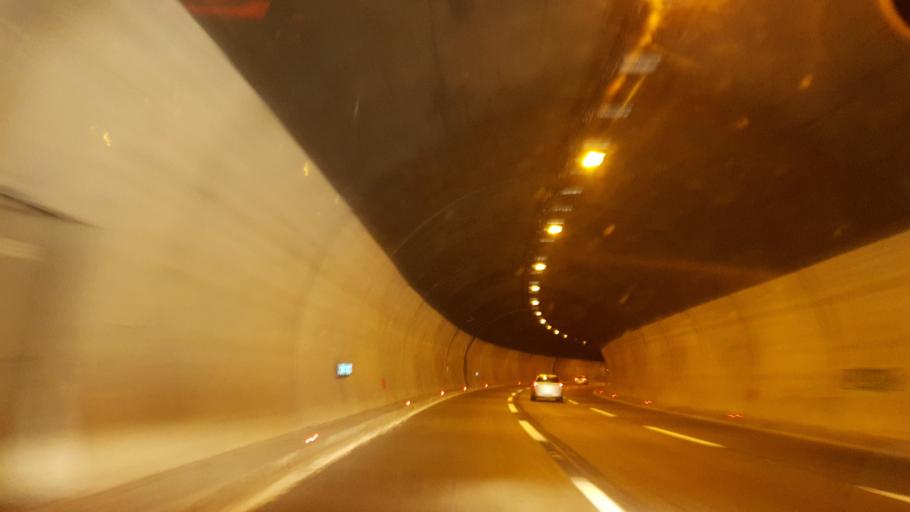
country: HR
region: Splitsko-Dalmatinska
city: Klis
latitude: 43.5491
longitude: 16.5349
